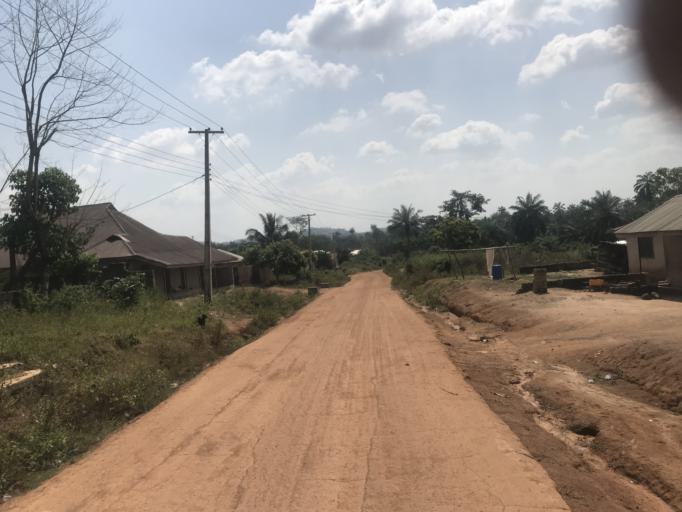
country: NG
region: Osun
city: Iragbiji
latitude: 7.8872
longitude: 4.7014
